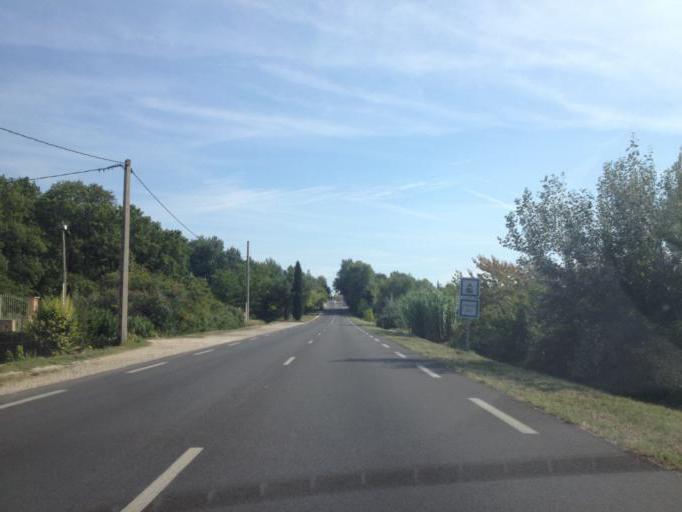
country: FR
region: Provence-Alpes-Cote d'Azur
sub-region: Departement du Vaucluse
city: Beaumes-de-Venise
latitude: 44.1108
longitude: 5.0198
